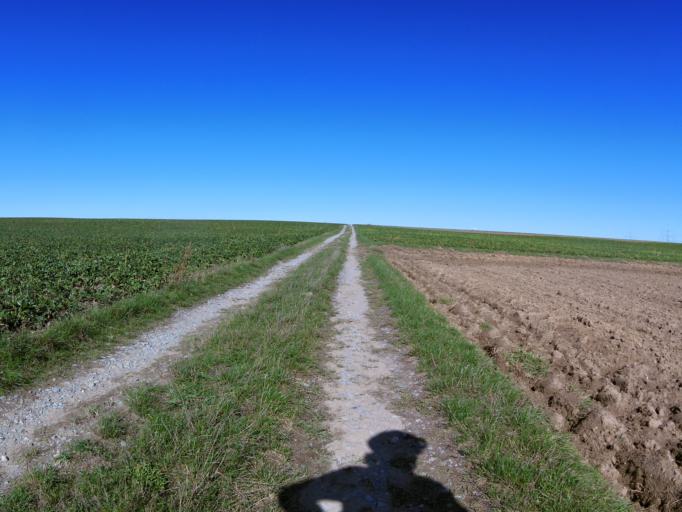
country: DE
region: Bavaria
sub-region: Regierungsbezirk Unterfranken
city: Theilheim
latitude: 49.7267
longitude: 10.0431
